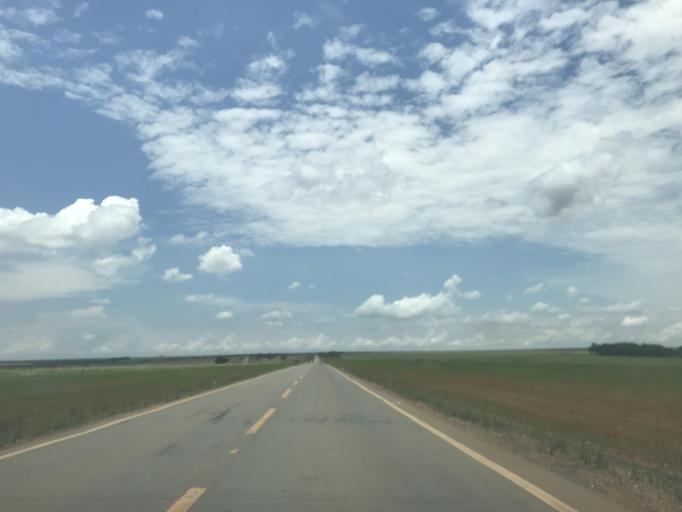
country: BR
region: Goias
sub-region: Luziania
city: Luziania
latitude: -16.4996
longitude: -48.2075
